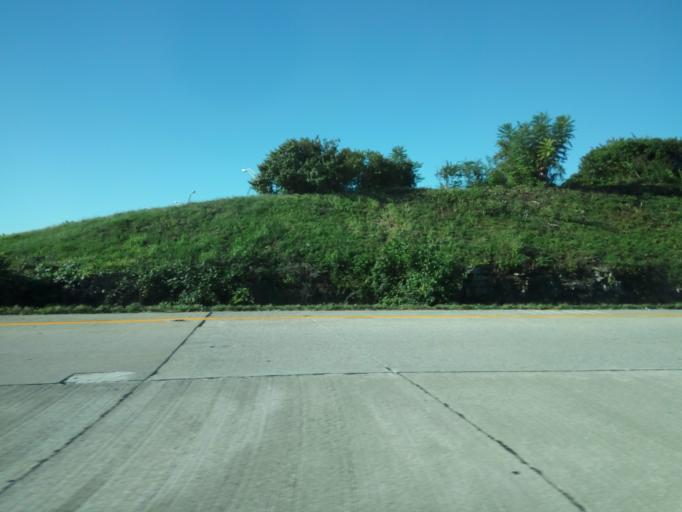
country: US
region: Kentucky
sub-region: Jefferson County
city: Audubon Park
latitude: 38.1906
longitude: -85.7326
